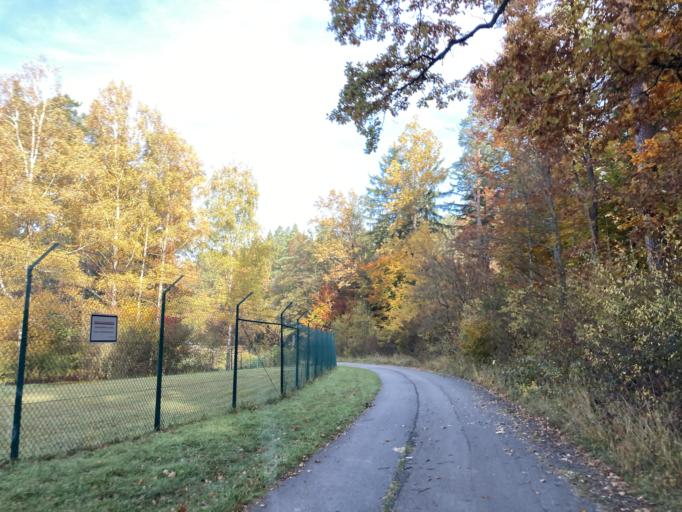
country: DE
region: Baden-Wuerttemberg
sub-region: Tuebingen Region
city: Bodelshausen
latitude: 48.4105
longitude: 8.9601
